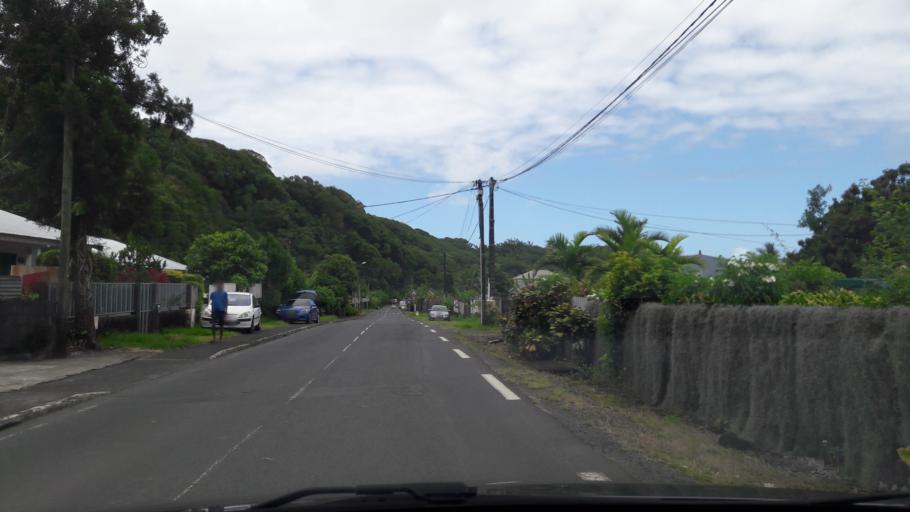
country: RE
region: Reunion
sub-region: Reunion
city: Saint-Andre
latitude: -20.9813
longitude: 55.6308
